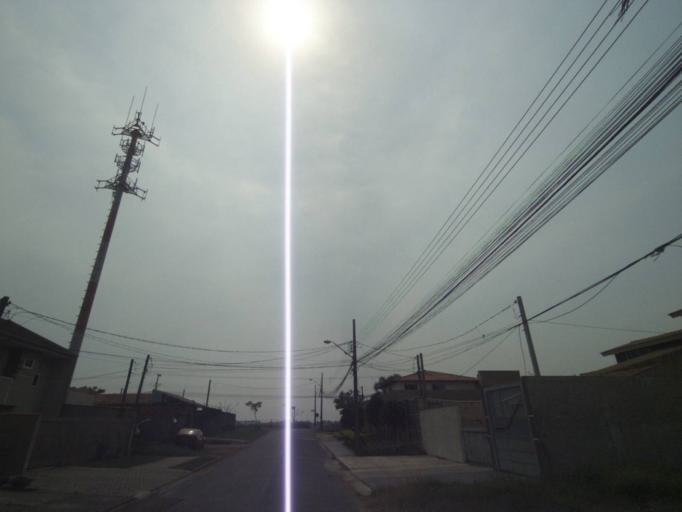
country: BR
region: Parana
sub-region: Sao Jose Dos Pinhais
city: Sao Jose dos Pinhais
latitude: -25.5170
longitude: -49.2804
